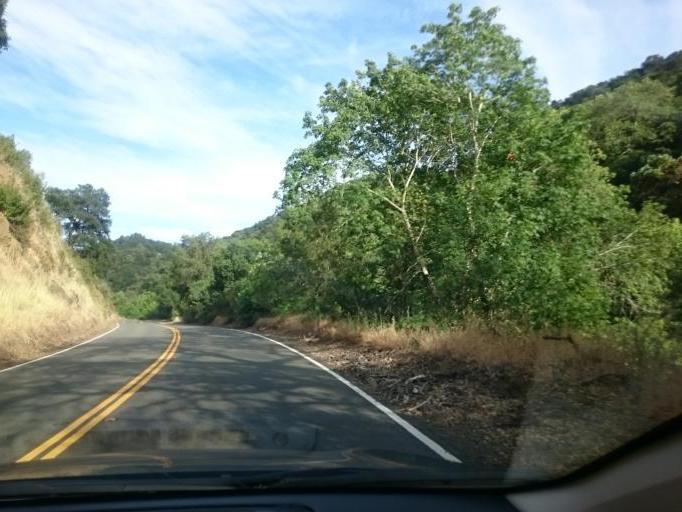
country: US
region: California
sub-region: Napa County
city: Yountville
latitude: 38.4881
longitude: -122.3192
